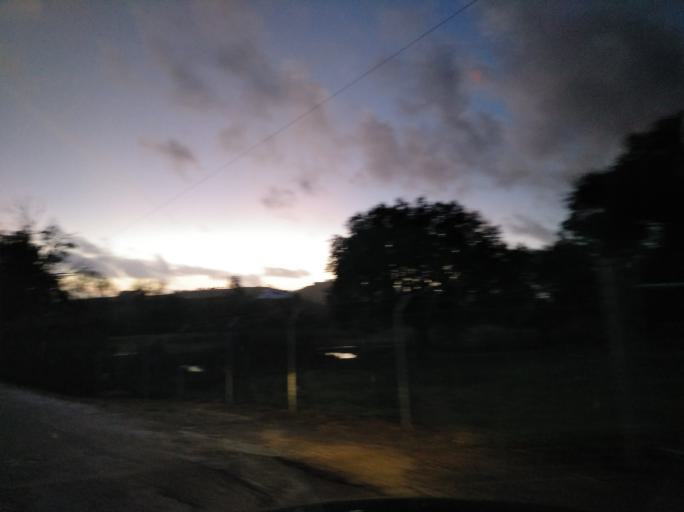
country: PT
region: Portalegre
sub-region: Campo Maior
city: Campo Maior
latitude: 39.0813
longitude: -7.0172
